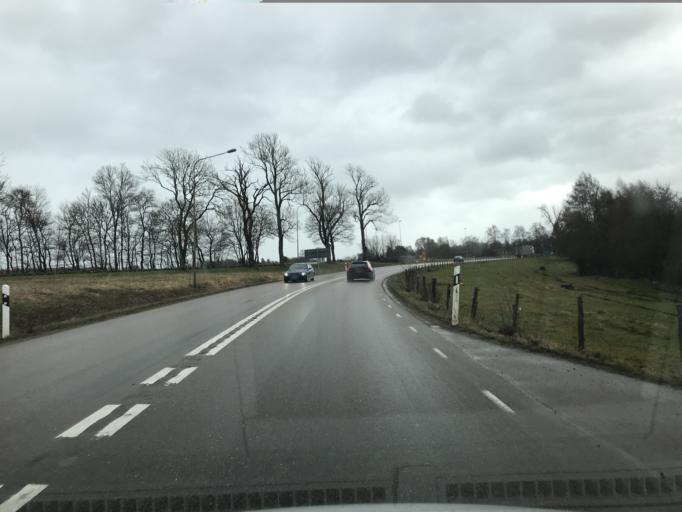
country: SE
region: Skane
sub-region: Klippans Kommun
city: Ljungbyhed
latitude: 56.0862
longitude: 13.2353
